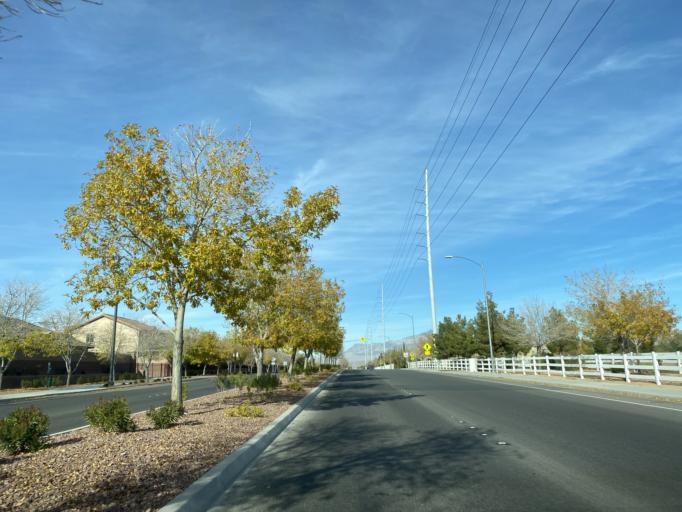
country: US
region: Nevada
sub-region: Clark County
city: Summerlin South
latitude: 36.3020
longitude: -115.3149
